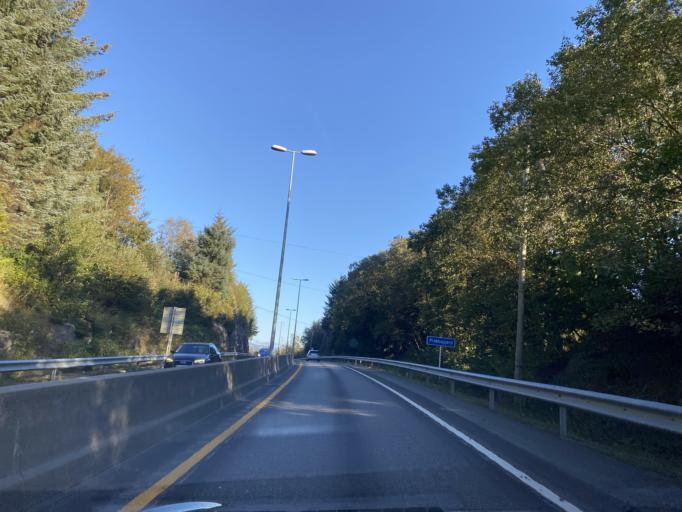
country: NO
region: Rogaland
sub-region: Karmoy
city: Eike
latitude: 59.4192
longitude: 5.3969
